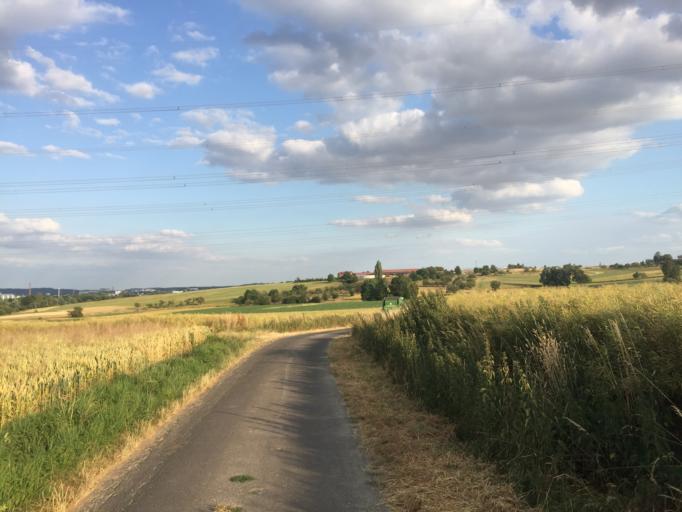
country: DE
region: Hesse
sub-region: Regierungsbezirk Giessen
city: Heuchelheim
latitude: 50.6029
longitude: 8.6093
